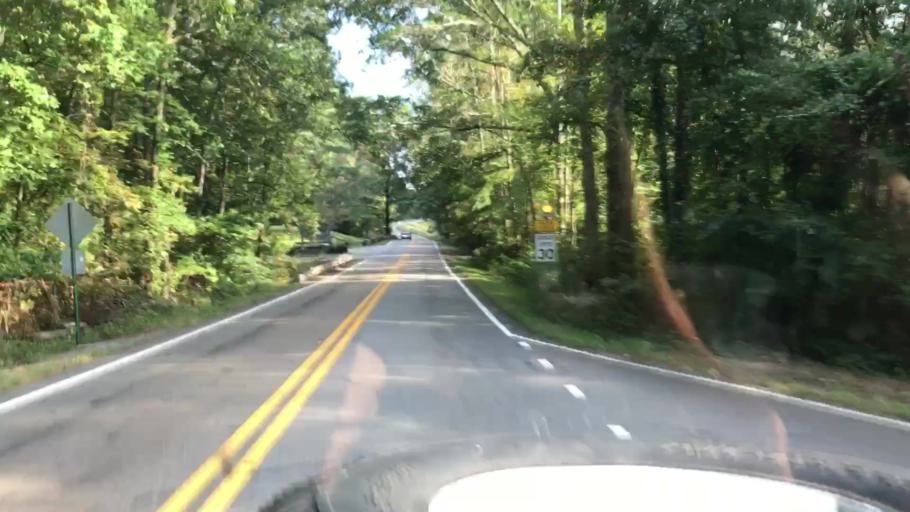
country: US
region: Georgia
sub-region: Forsyth County
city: Cumming
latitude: 34.1767
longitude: -84.0807
